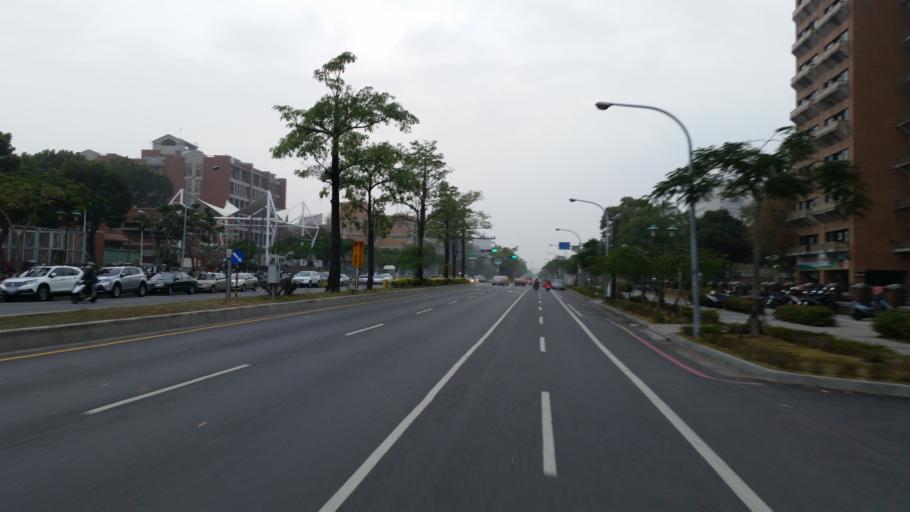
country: TW
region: Taiwan
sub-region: Tainan
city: Tainan
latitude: 23.0007
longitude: 120.2237
